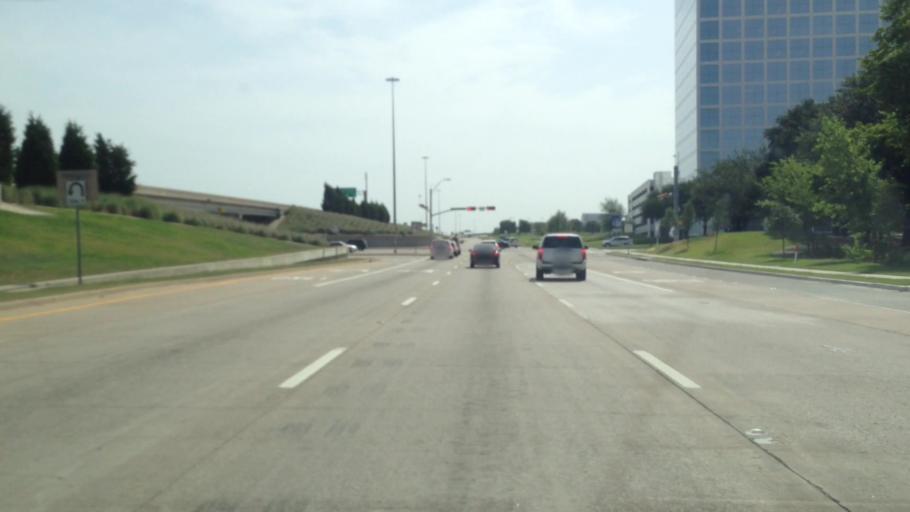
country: US
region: Texas
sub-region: Denton County
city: The Colony
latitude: 33.0857
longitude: -96.8400
